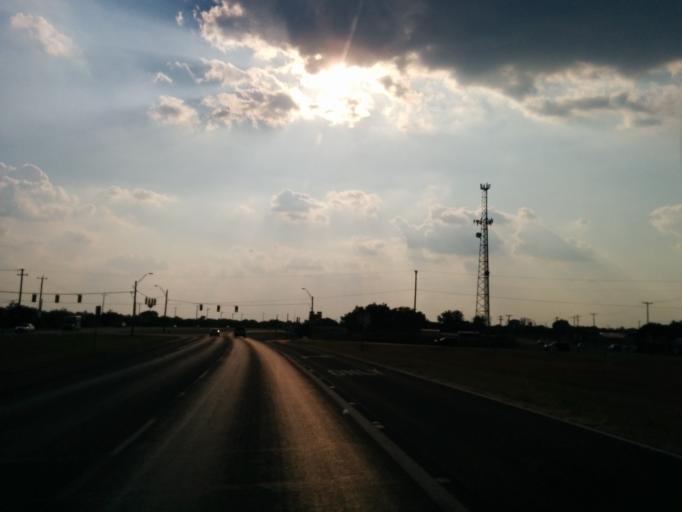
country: US
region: Texas
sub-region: Bexar County
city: Saint Hedwig
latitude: 29.3664
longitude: -98.2435
